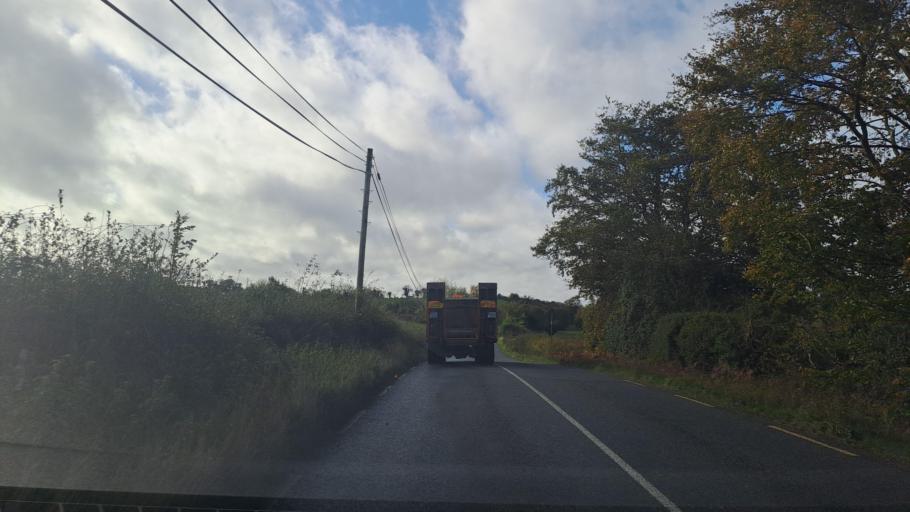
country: IE
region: Ulster
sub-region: County Monaghan
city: Monaghan
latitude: 54.1171
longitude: -6.9250
